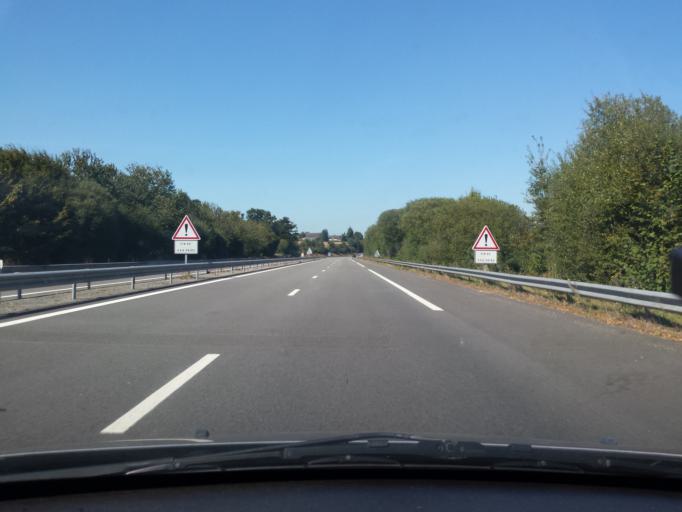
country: FR
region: Brittany
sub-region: Departement du Morbihan
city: Saint-Thuriau
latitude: 48.0014
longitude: -2.8964
